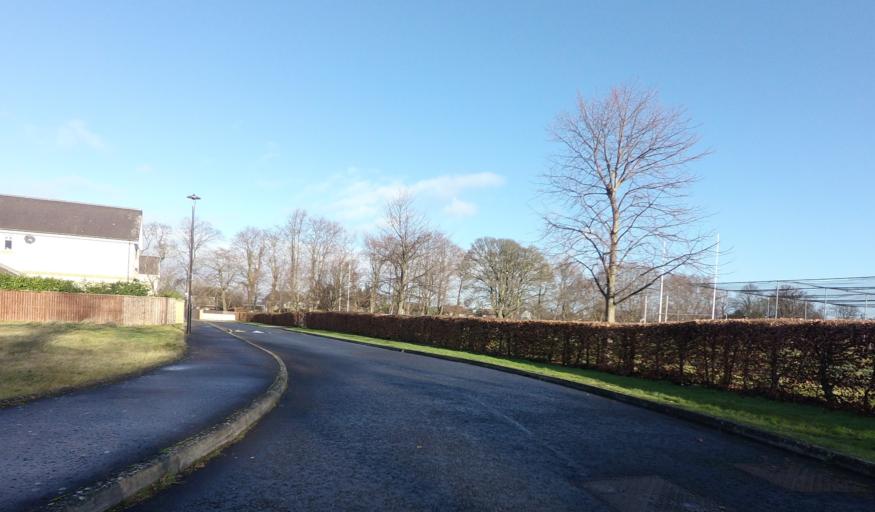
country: GB
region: Scotland
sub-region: Edinburgh
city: Currie
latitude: 55.9695
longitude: -3.3026
